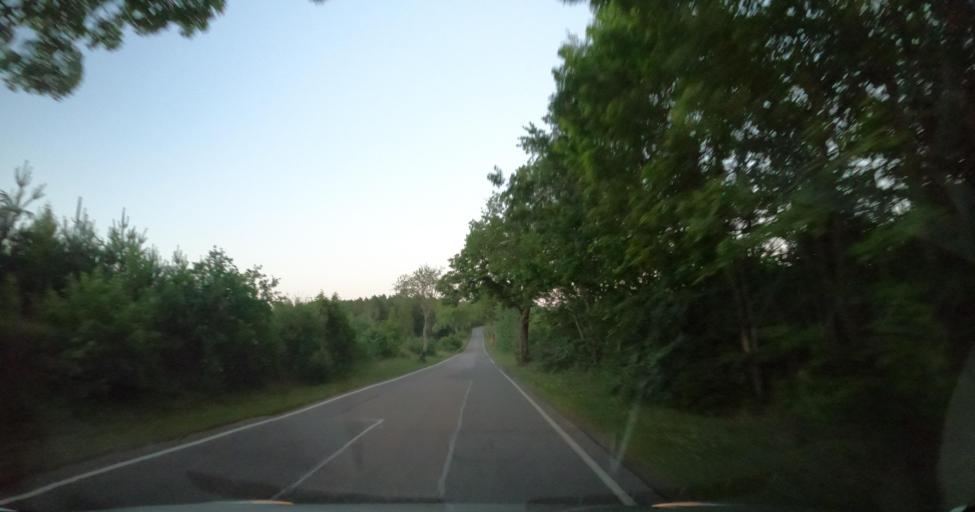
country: PL
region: Pomeranian Voivodeship
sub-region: Powiat wejherowski
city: Luzino
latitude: 54.4648
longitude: 18.1212
